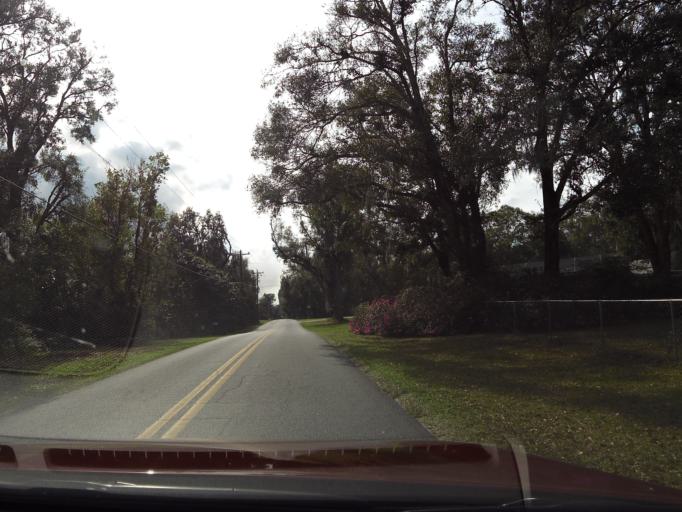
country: US
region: Florida
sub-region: Volusia County
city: De Leon Springs
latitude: 29.1400
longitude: -81.3210
